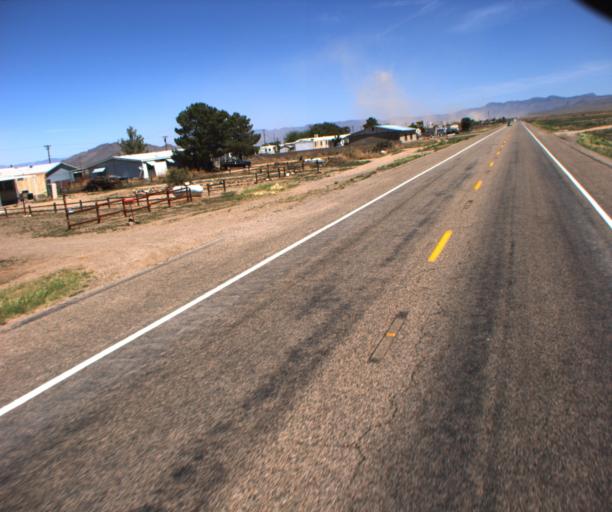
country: US
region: Arizona
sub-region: Mohave County
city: New Kingman-Butler
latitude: 35.2918
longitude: -113.9394
